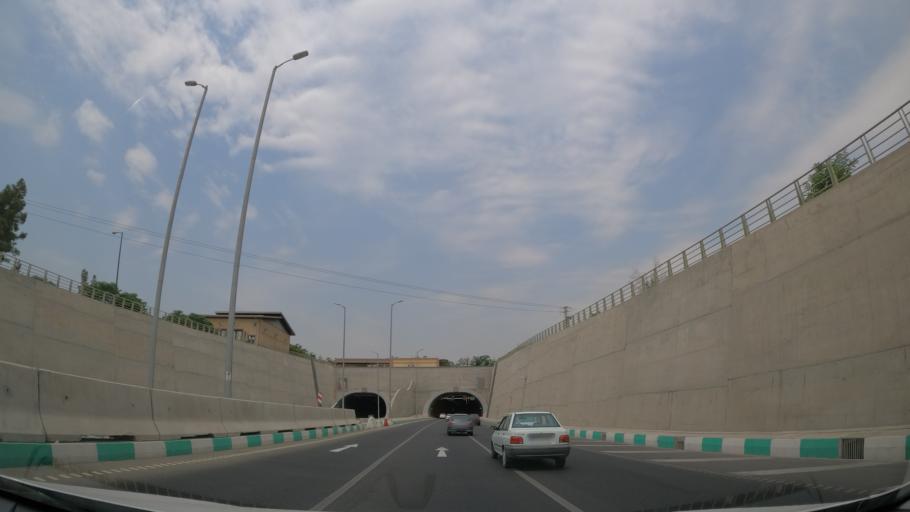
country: IR
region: Tehran
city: Shahr-e Qods
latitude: 35.7404
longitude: 51.2101
